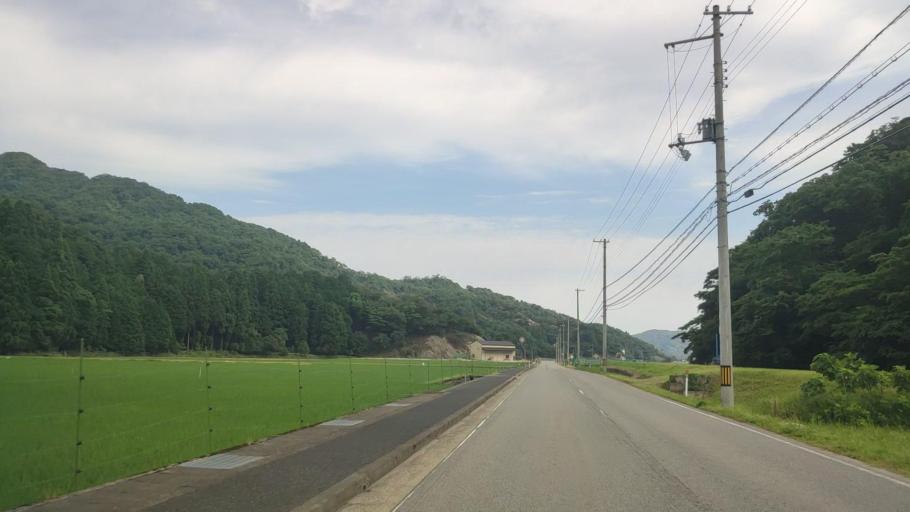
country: JP
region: Hyogo
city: Toyooka
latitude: 35.6181
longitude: 134.8427
